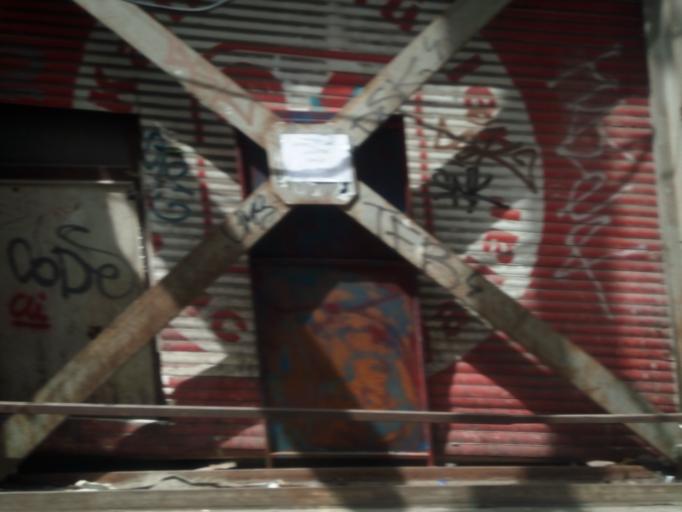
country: TR
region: Istanbul
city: Eminoenue
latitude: 41.0139
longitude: 28.9767
